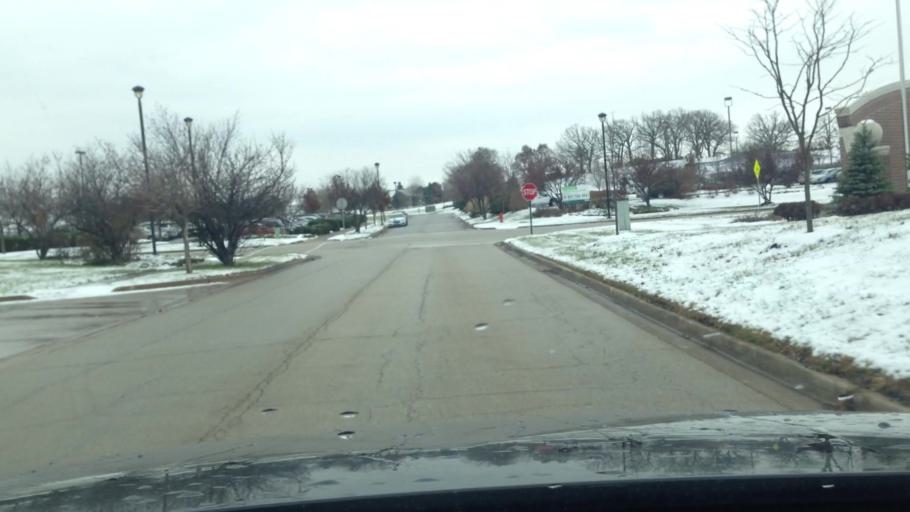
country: US
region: Illinois
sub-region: McHenry County
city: Huntley
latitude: 42.1490
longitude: -88.4345
